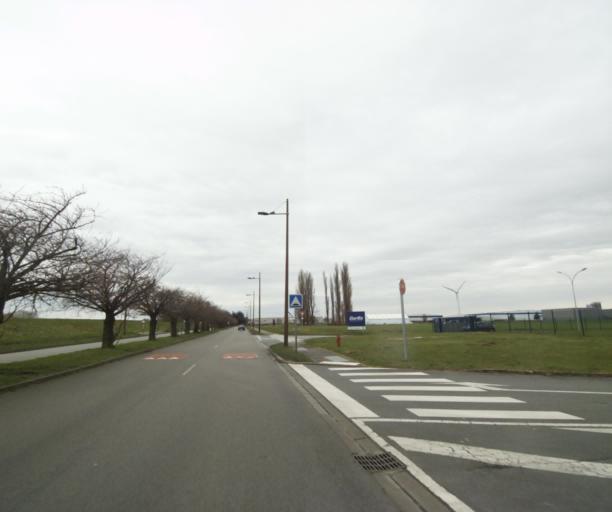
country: FR
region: Nord-Pas-de-Calais
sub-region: Departement du Nord
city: Quarouble
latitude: 50.3779
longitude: 3.6141
